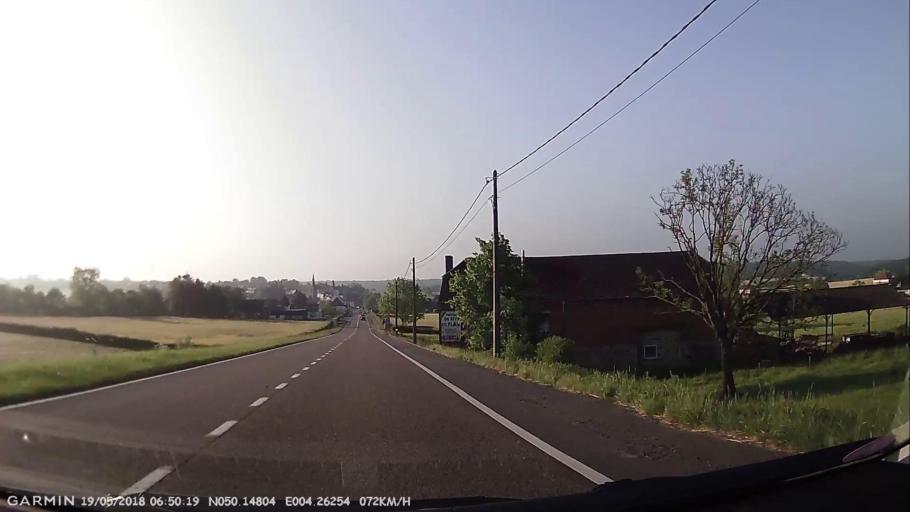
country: BE
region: Wallonia
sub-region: Province du Hainaut
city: Froidchapelle
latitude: 50.1479
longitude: 4.2627
